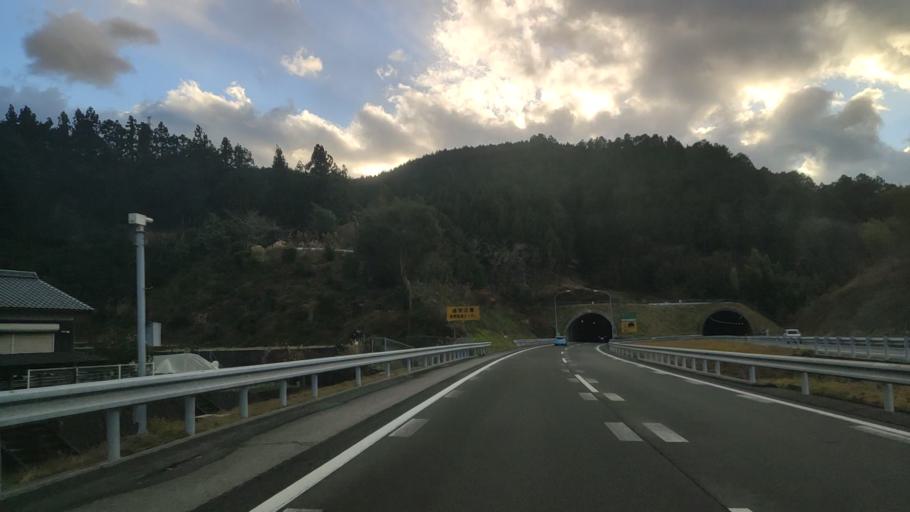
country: JP
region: Ehime
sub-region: Shikoku-chuo Shi
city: Matsuyama
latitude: 33.7922
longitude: 132.9255
